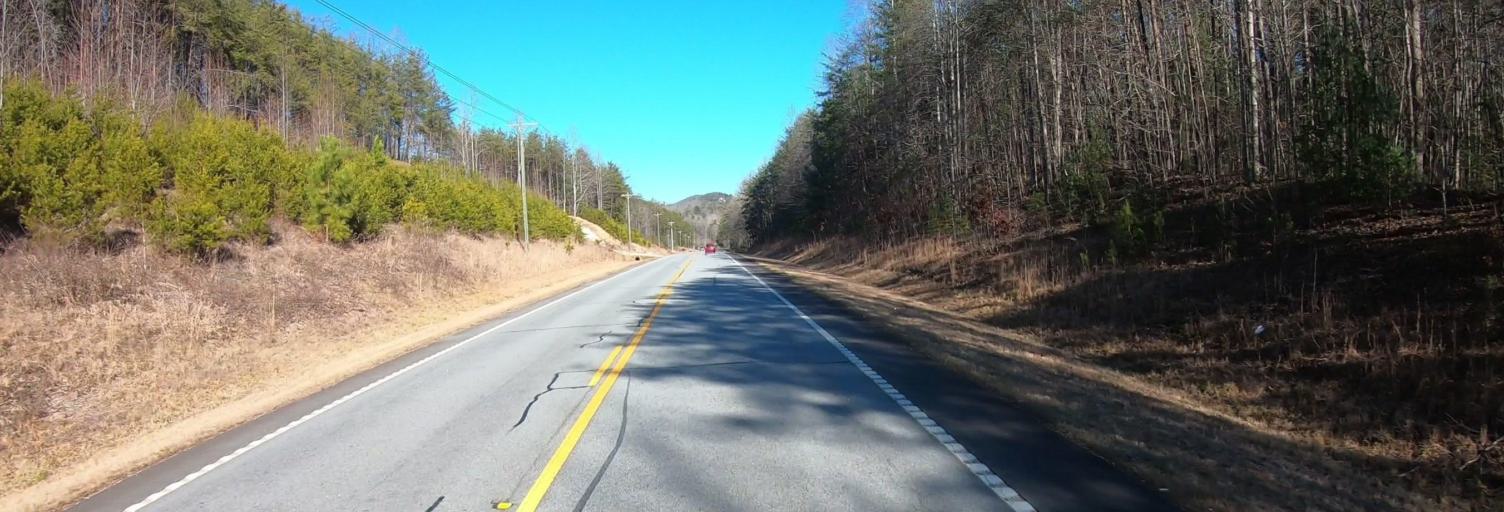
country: US
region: South Carolina
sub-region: Pickens County
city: Pickens
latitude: 34.9727
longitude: -82.8073
